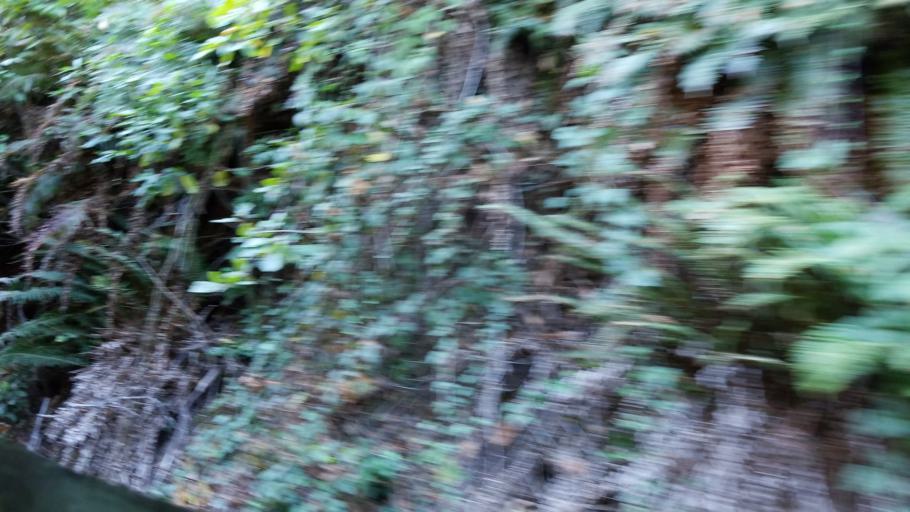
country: US
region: California
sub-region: Mendocino County
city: Fort Bragg
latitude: 39.4483
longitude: -123.7960
